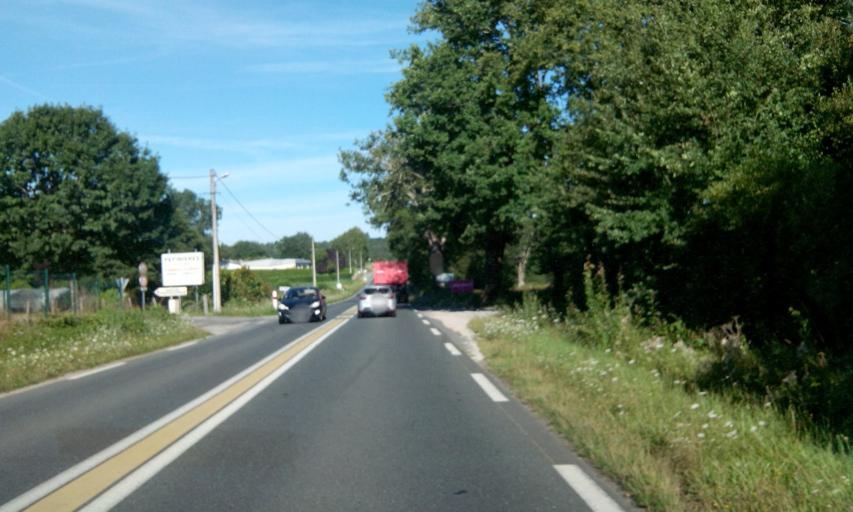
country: FR
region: Limousin
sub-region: Departement de la Haute-Vienne
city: Saint-Leonard-de-Noblat
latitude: 45.8471
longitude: 1.4551
